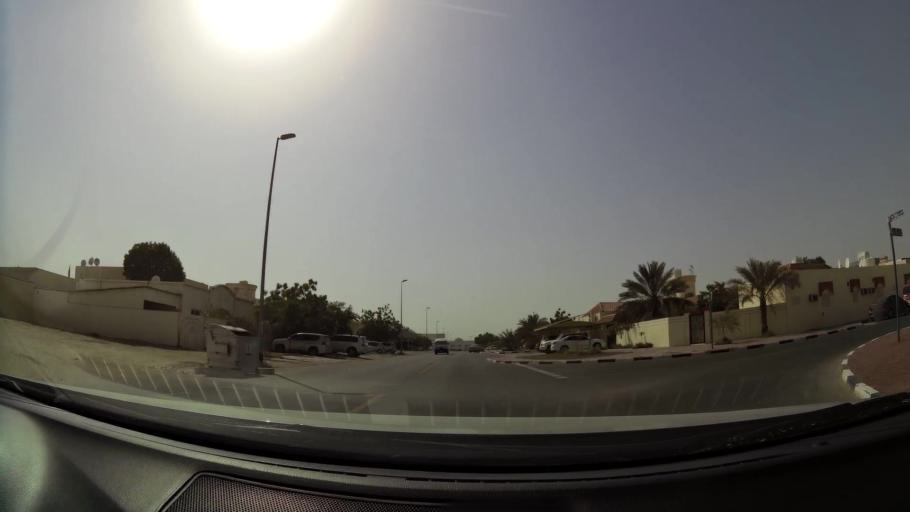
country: AE
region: Dubai
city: Dubai
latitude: 25.1708
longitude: 55.2497
